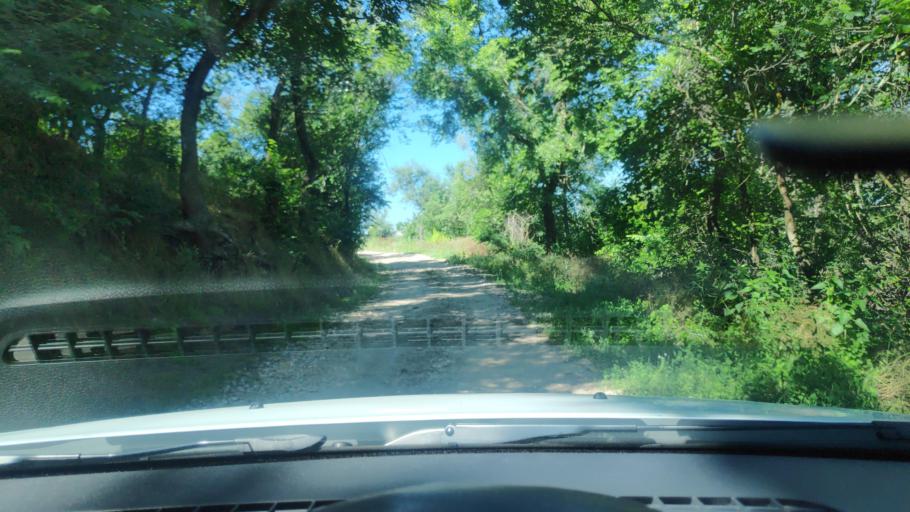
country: MK
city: Klechovce
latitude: 42.0726
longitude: 21.8982
